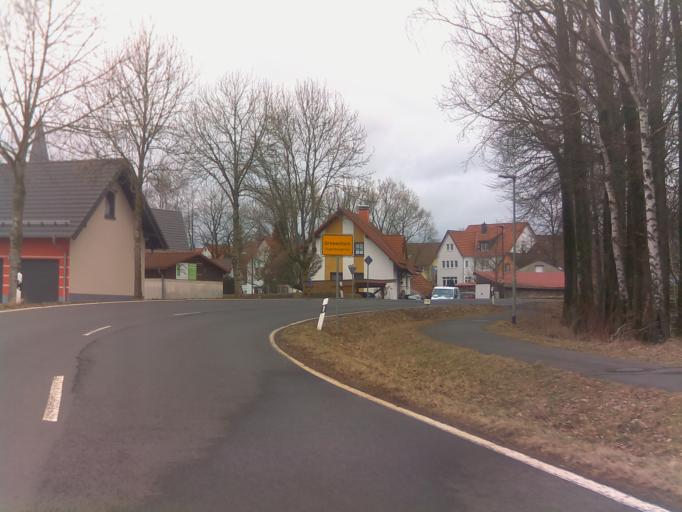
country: DE
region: Hesse
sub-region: Regierungsbezirk Giessen
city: Grebenhain
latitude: 50.4875
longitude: 9.3388
